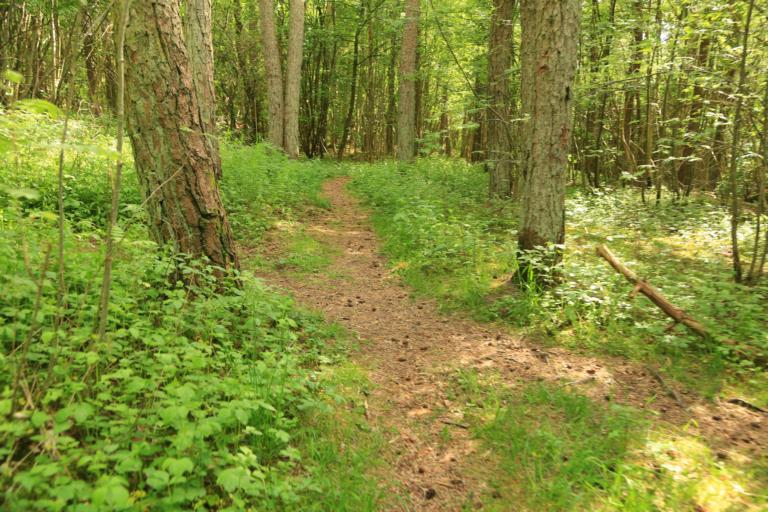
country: SE
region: Halland
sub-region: Varbergs Kommun
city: Varberg
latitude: 57.1074
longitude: 12.2835
